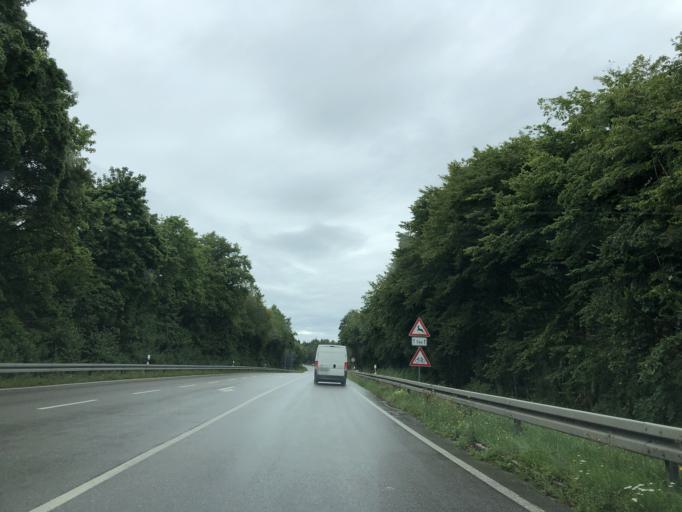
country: DE
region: Bavaria
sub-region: Upper Bavaria
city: Taufkirchen
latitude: 48.0258
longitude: 11.6356
